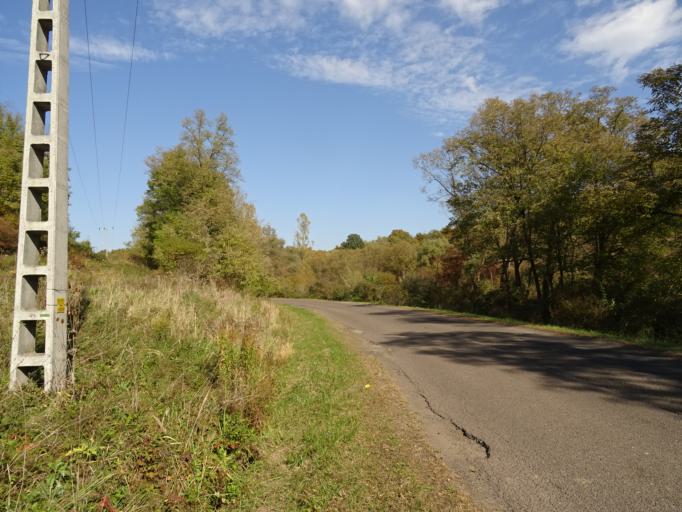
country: HU
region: Nograd
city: Salgotarjan
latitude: 48.0457
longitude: 19.7530
